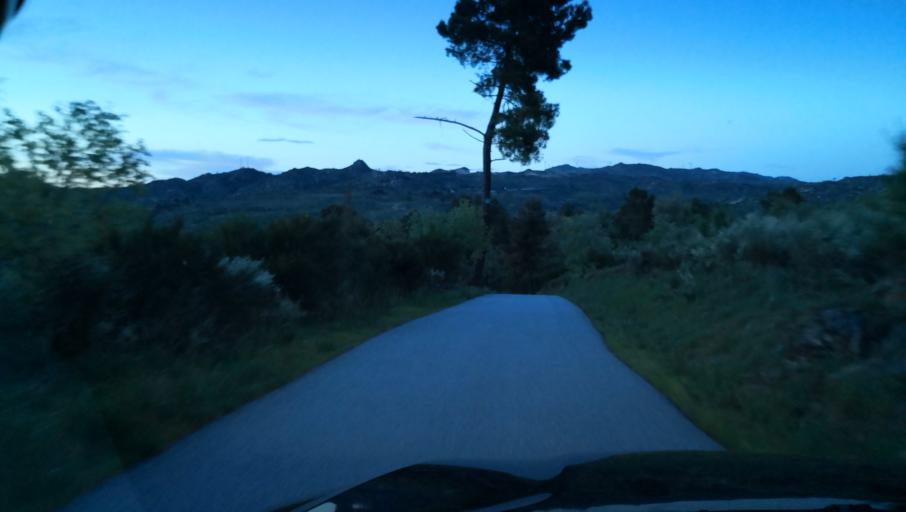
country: PT
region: Vila Real
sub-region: Vila Real
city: Vila Real
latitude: 41.3515
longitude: -7.6903
